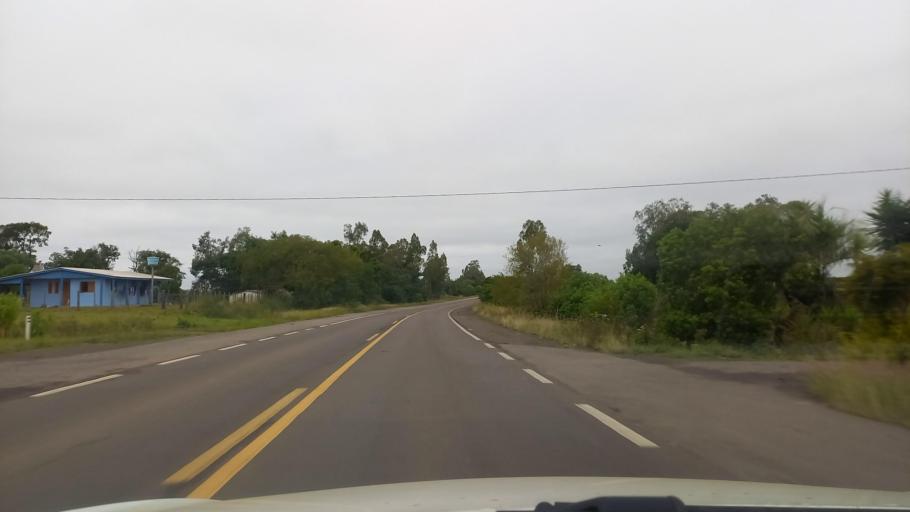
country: BR
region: Rio Grande do Sul
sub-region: Sao Pedro Do Sul
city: Sao Pedro do Sul
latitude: -29.7952
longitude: -54.1193
